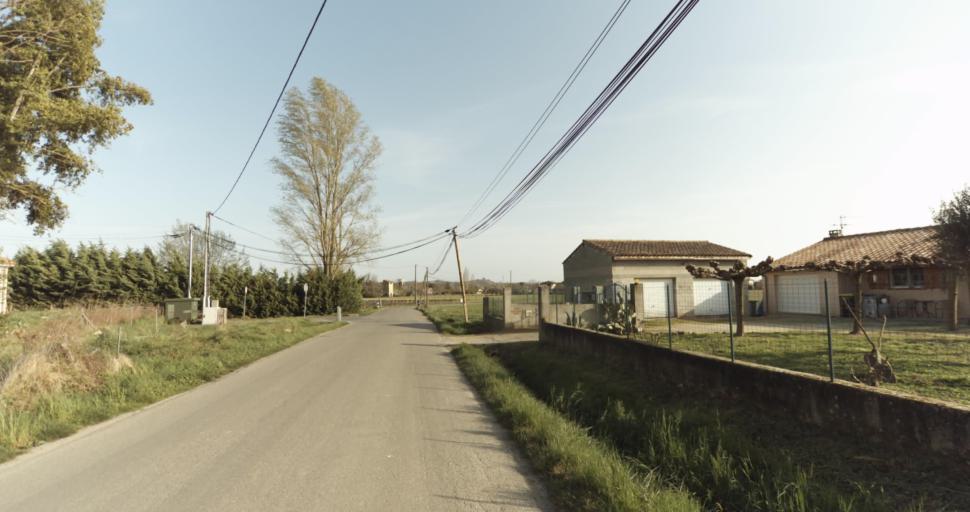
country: FR
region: Midi-Pyrenees
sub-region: Departement du Tarn
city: Saint-Sulpice-la-Pointe
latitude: 43.7660
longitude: 1.6770
